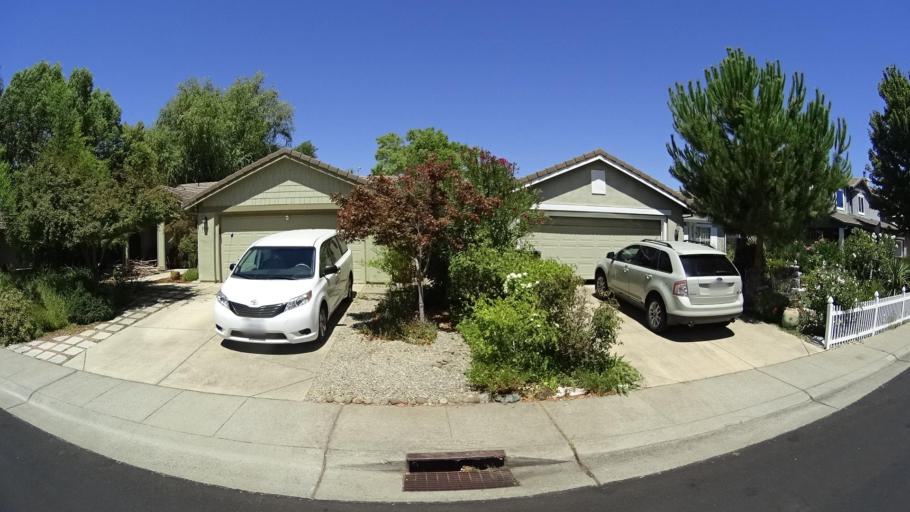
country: US
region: California
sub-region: Placer County
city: Rocklin
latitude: 38.8142
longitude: -121.2754
